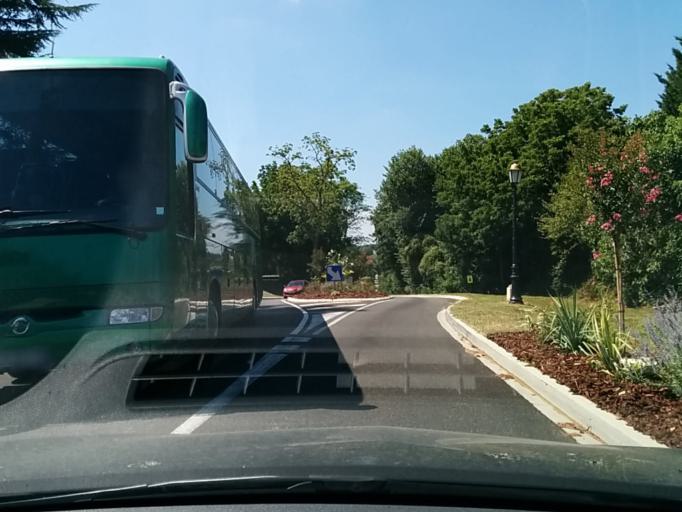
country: FR
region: Midi-Pyrenees
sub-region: Departement du Gers
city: Le Houga
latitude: 43.7697
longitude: -0.1243
